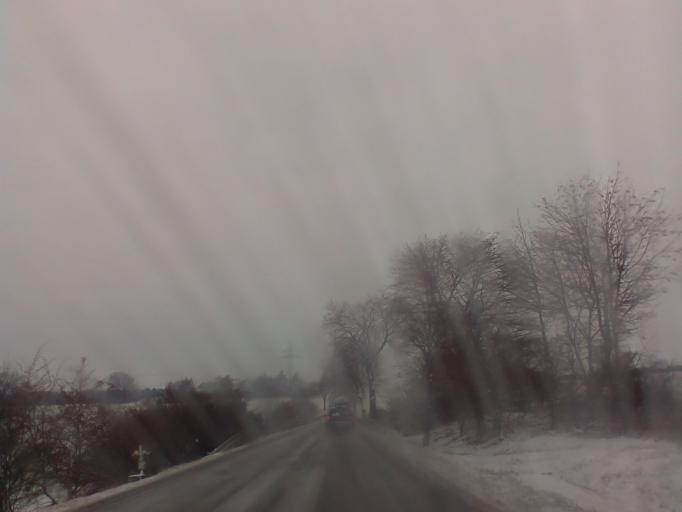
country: DE
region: Thuringia
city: Stadtilm
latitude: 50.7866
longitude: 11.0619
